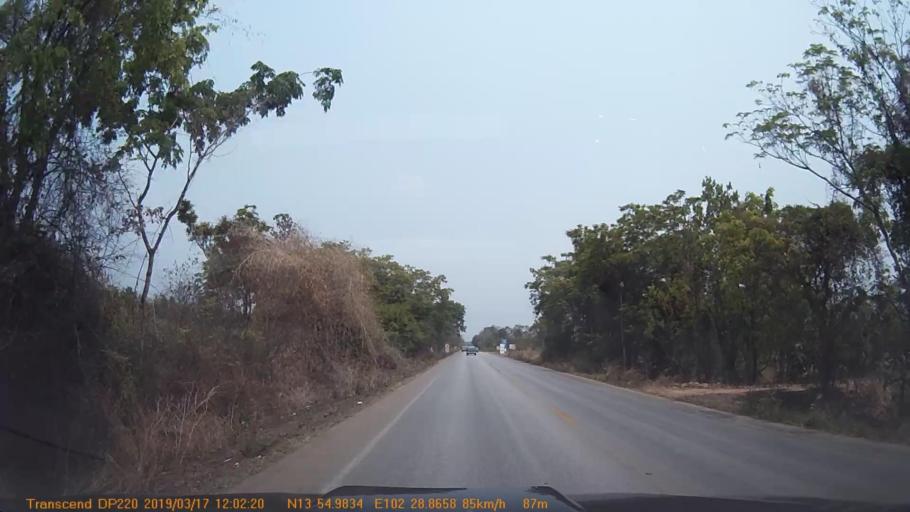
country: TH
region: Sa Kaeo
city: Khok Sung
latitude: 13.9167
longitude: 102.4812
